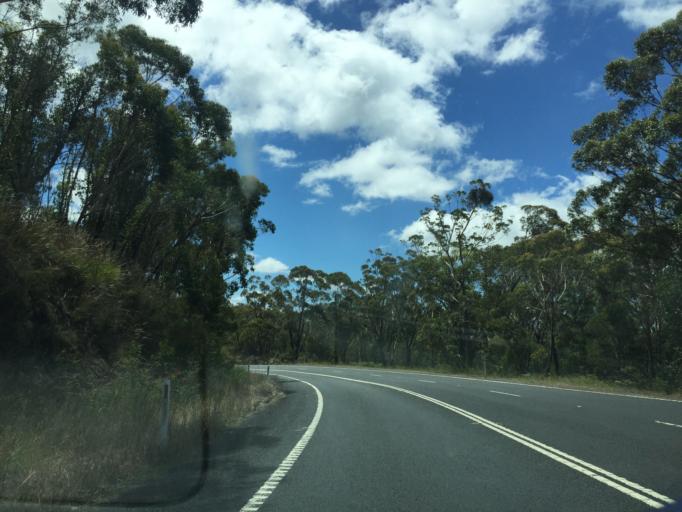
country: AU
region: New South Wales
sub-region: Blue Mountains Municipality
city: Blackheath
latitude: -33.5587
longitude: 150.3441
